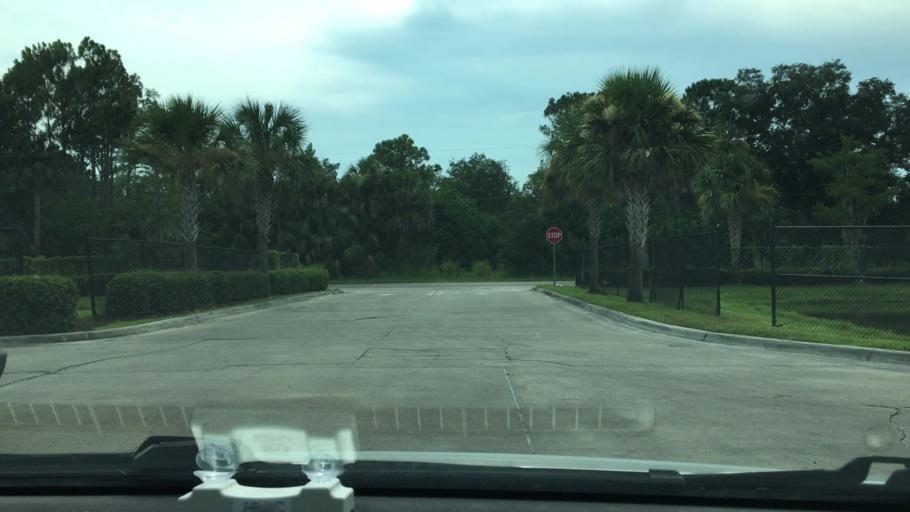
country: US
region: Florida
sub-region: Seminole County
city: Midway
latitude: 28.7864
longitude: -81.2141
